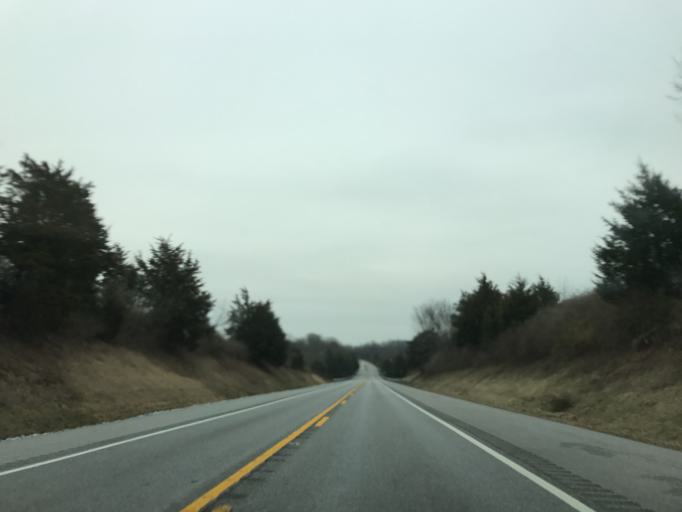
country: US
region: Maryland
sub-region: Carroll County
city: Taneytown
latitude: 39.6410
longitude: -77.1270
